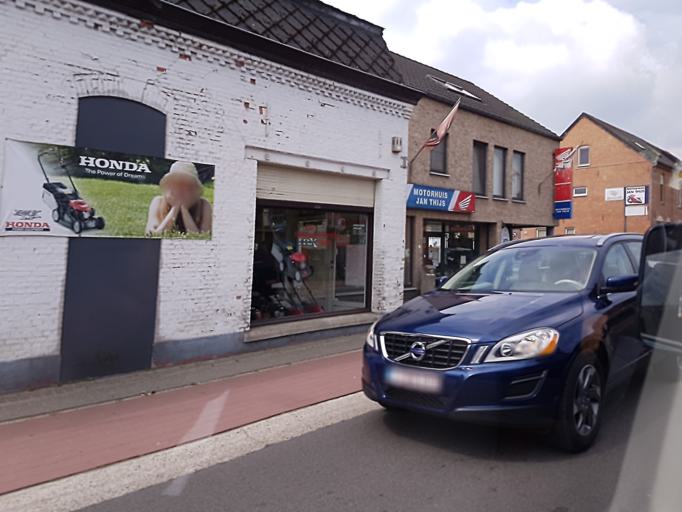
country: BE
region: Flanders
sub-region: Provincie Limburg
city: Neerpelt
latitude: 51.2276
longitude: 5.4813
